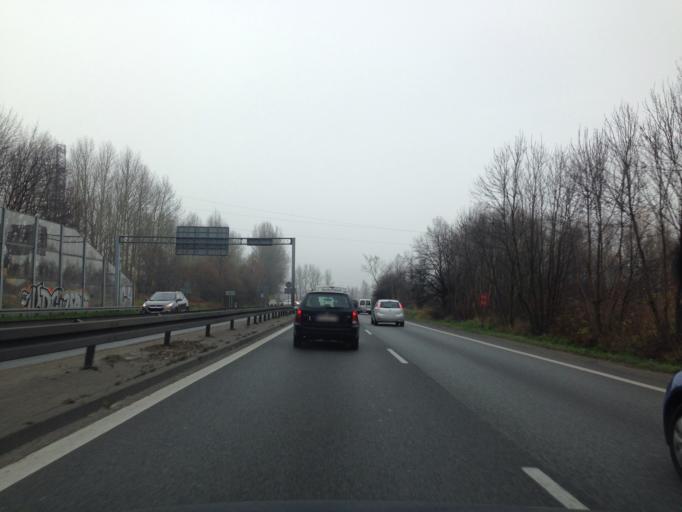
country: PL
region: Silesian Voivodeship
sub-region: Powiat bedzinski
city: Bedzin
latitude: 50.3130
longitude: 19.1106
